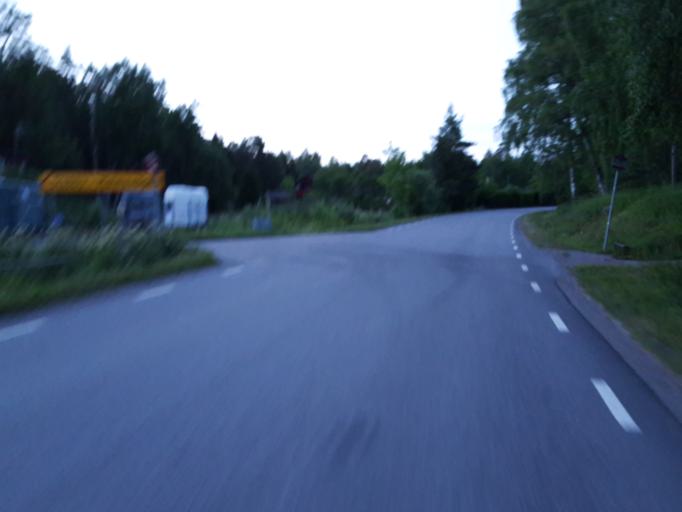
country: SE
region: Uppsala
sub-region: Uppsala Kommun
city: Uppsala
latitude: 59.8019
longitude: 17.5904
